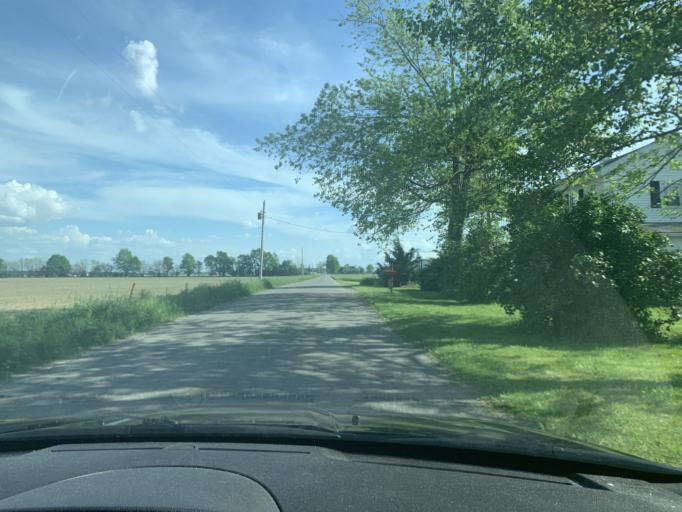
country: US
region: Ohio
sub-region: Logan County
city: De Graff
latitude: 40.2625
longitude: -84.0159
